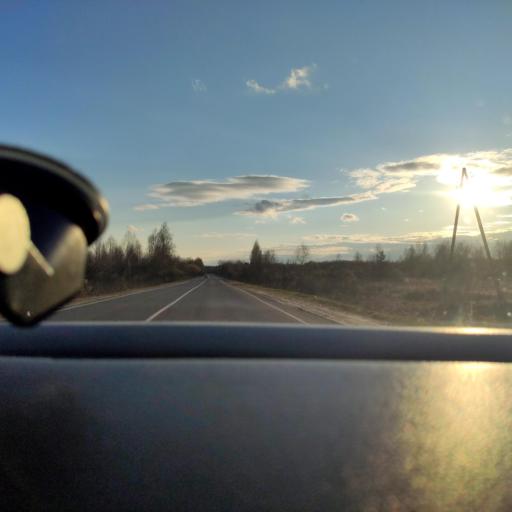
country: RU
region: Moskovskaya
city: Shaturtorf
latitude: 55.4328
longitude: 39.4078
